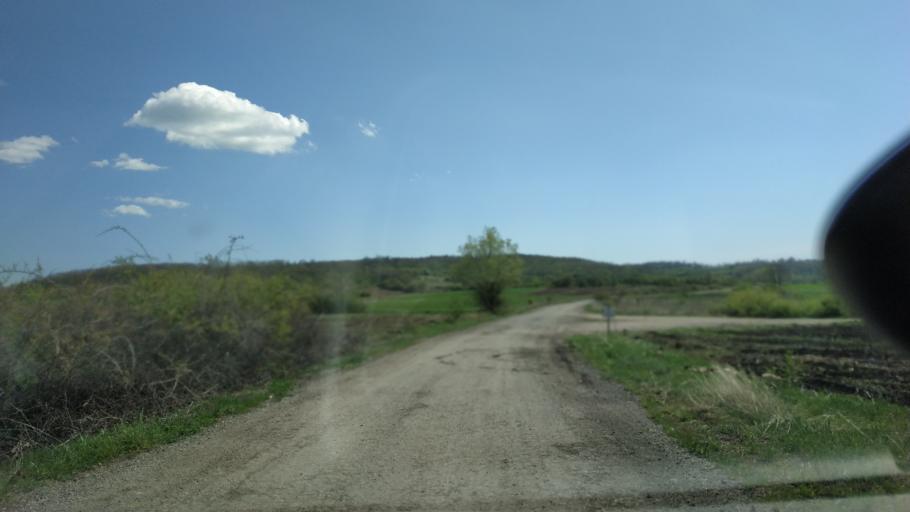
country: RS
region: Central Serbia
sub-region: Zajecarski Okrug
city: Soko Banja
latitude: 43.5156
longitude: 21.9057
